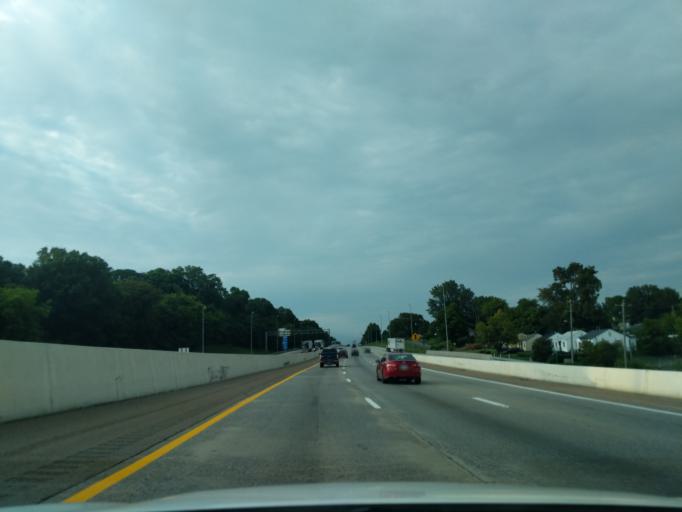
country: US
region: Tennessee
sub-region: Shelby County
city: New South Memphis
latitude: 35.0881
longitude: -90.0766
